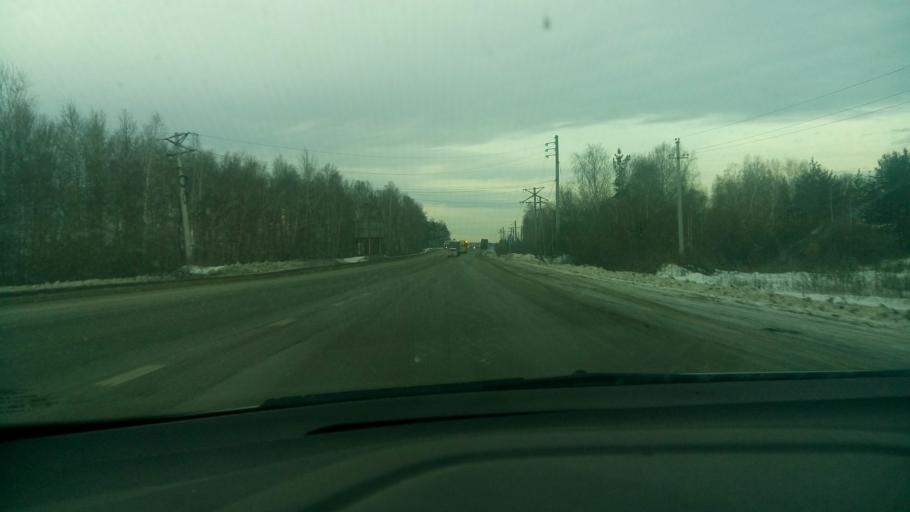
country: RU
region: Sverdlovsk
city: Istok
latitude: 56.7575
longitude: 60.7636
